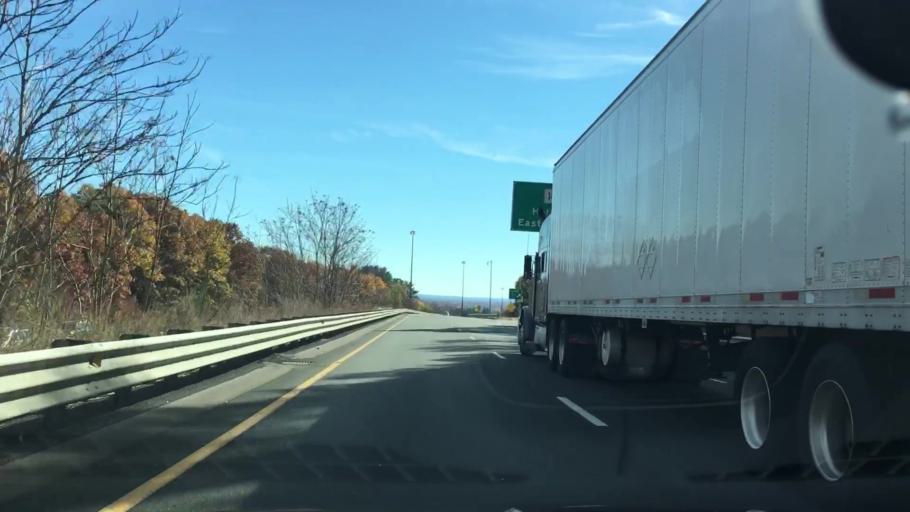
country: US
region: Massachusetts
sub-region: Hampden County
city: Holyoke
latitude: 42.2201
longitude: -72.6348
